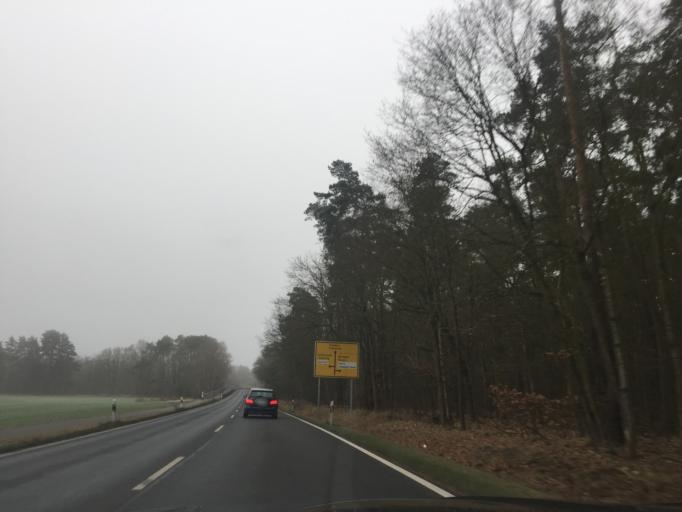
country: DE
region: Brandenburg
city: Falkensee
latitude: 52.6113
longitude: 13.1215
